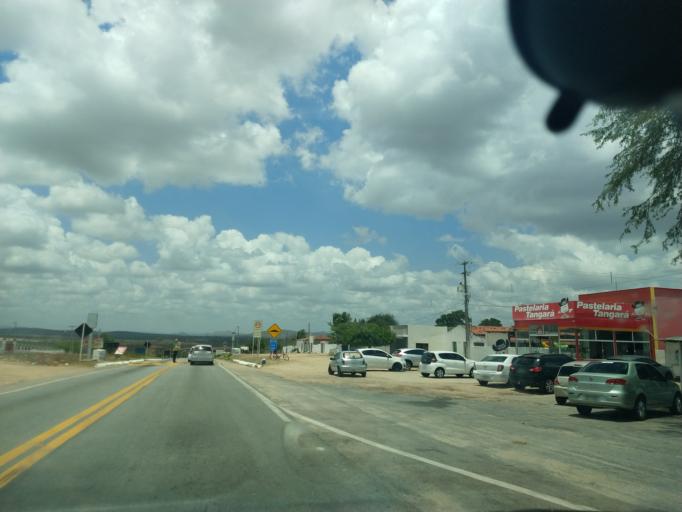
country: BR
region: Rio Grande do Norte
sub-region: Tangara
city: Tangara
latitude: -6.2027
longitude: -35.8048
